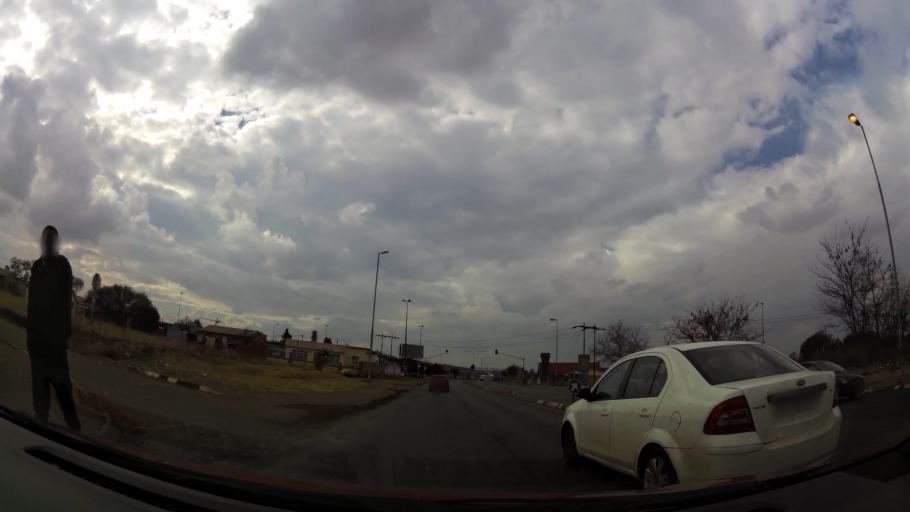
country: ZA
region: Gauteng
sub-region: City of Johannesburg Metropolitan Municipality
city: Soweto
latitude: -26.2395
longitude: 27.8583
